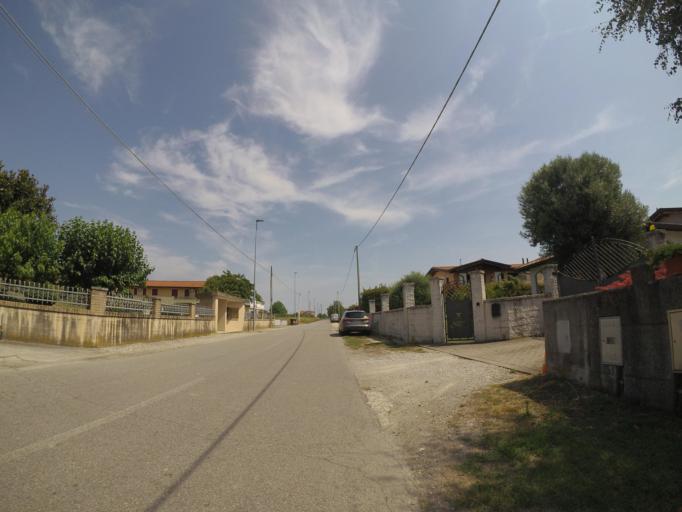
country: IT
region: Friuli Venezia Giulia
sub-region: Provincia di Pordenone
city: Rosa
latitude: 45.9289
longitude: 12.8854
